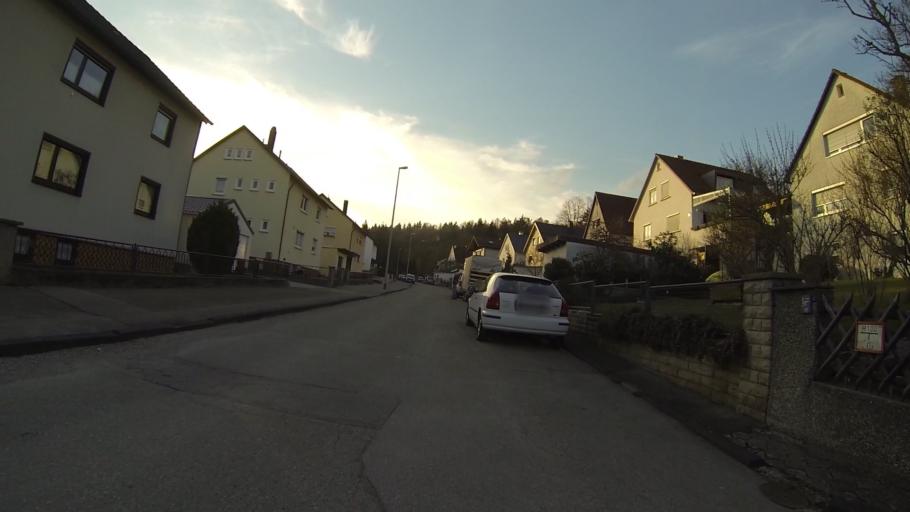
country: DE
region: Baden-Wuerttemberg
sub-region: Regierungsbezirk Stuttgart
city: Heidenheim an der Brenz
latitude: 48.7028
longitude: 10.1514
